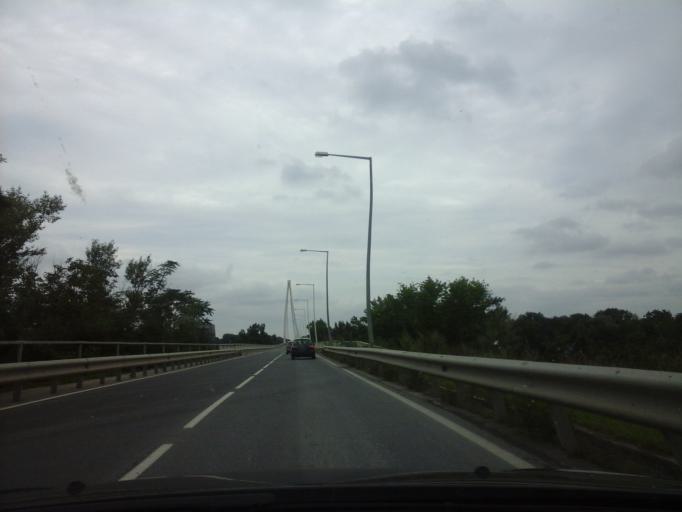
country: AT
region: Lower Austria
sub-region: Politischer Bezirk Bruck an der Leitha
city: Bad Deutsch-Altenburg
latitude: 48.1408
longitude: 16.9121
